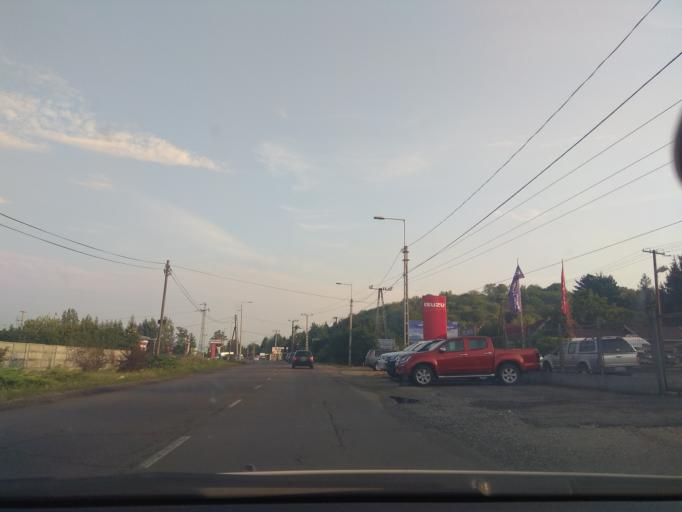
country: HU
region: Heves
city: Andornaktalya
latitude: 47.8707
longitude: 20.4043
